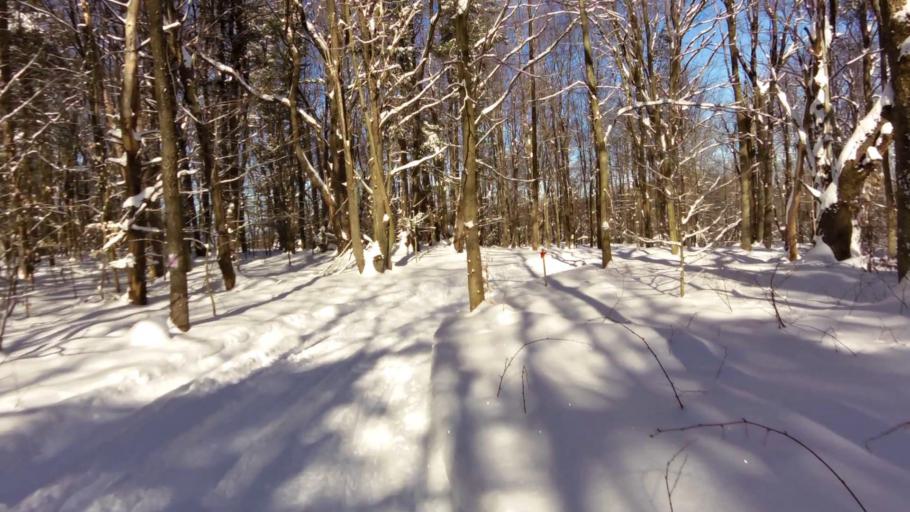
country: US
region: New York
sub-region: Chautauqua County
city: Fredonia
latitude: 42.3479
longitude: -79.1932
